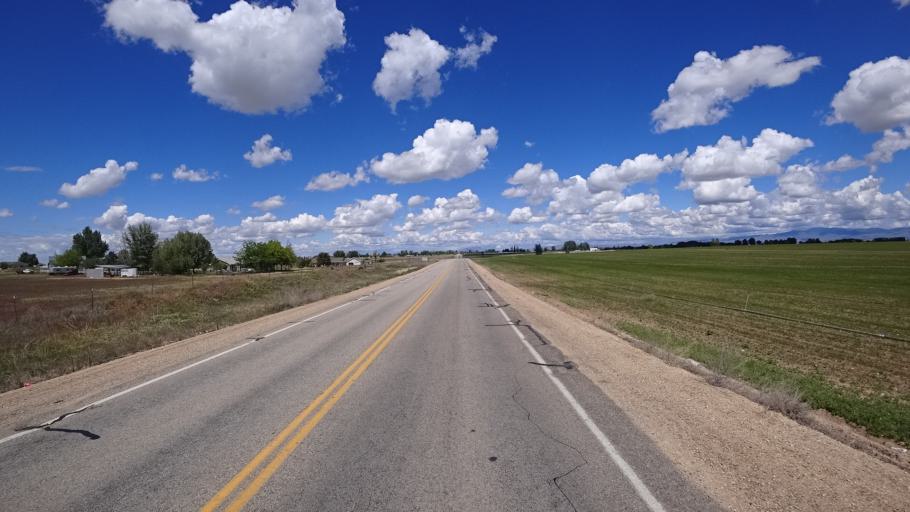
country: US
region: Idaho
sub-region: Ada County
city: Meridian
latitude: 43.5657
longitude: -116.4342
